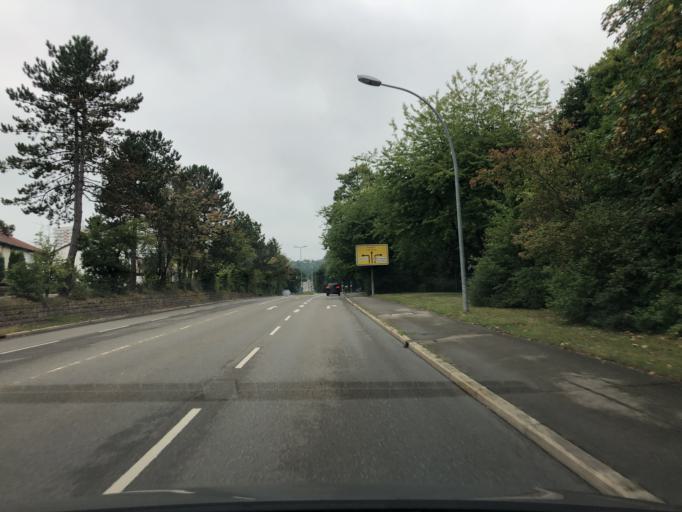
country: DE
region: Baden-Wuerttemberg
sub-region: Regierungsbezirk Stuttgart
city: Sindelfingen
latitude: 48.7231
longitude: 9.0090
